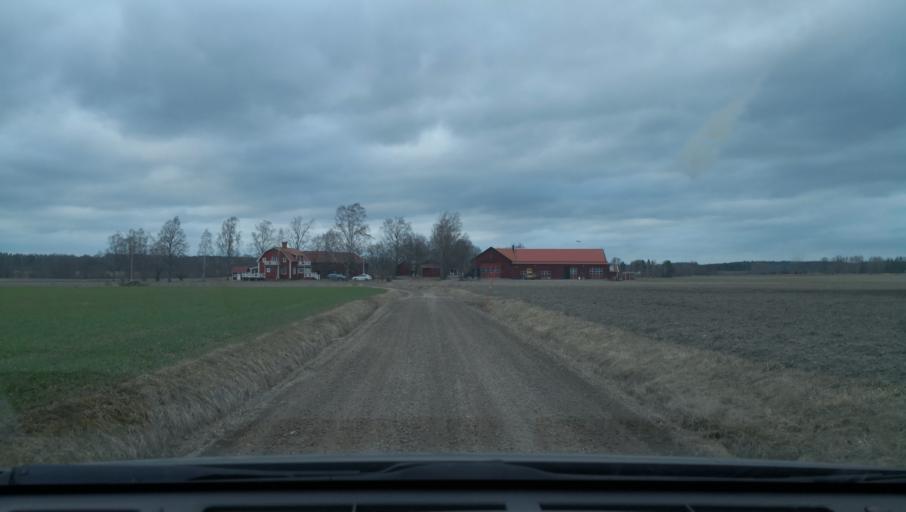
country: SE
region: Vaestmanland
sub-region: Kopings Kommun
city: Kolsva
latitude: 59.5333
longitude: 15.8933
